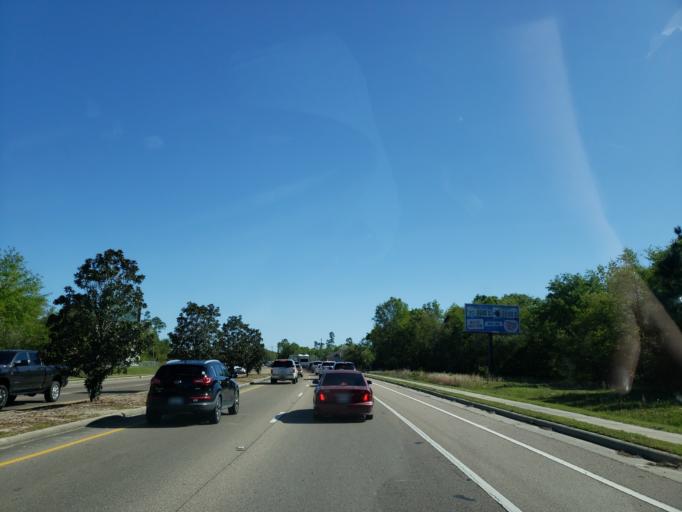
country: US
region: Mississippi
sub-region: Harrison County
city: West Gulfport
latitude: 30.4197
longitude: -89.0323
